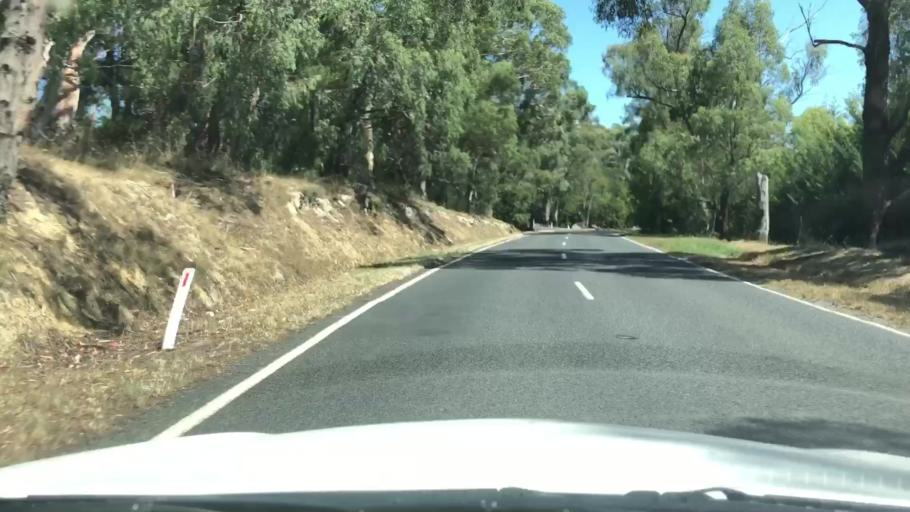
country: AU
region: Victoria
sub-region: Yarra Ranges
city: Woori Yallock
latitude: -37.7996
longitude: 145.5260
